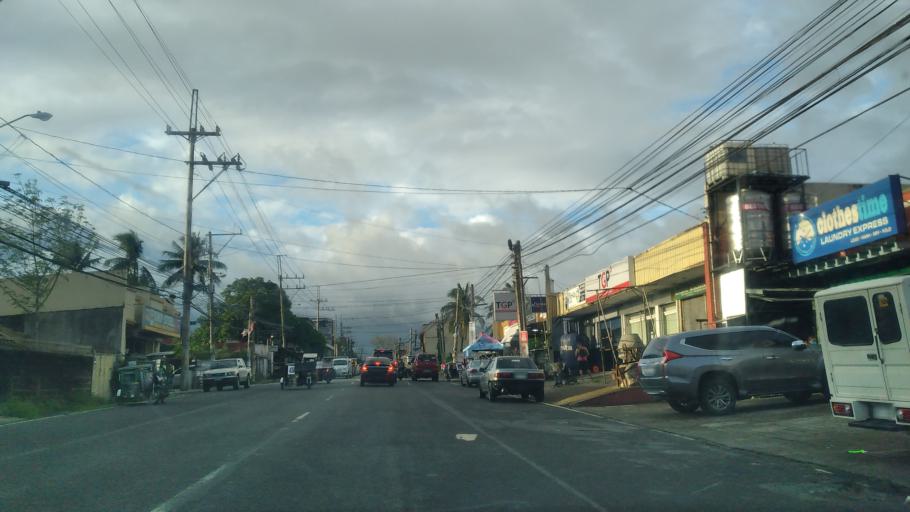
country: PH
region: Calabarzon
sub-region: Province of Quezon
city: Lucena
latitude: 13.9512
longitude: 121.6132
